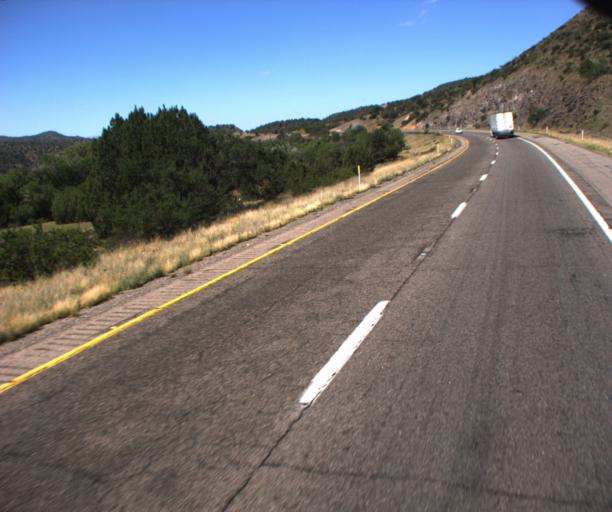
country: US
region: Arizona
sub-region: Mohave County
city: Peach Springs
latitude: 35.1845
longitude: -113.4648
